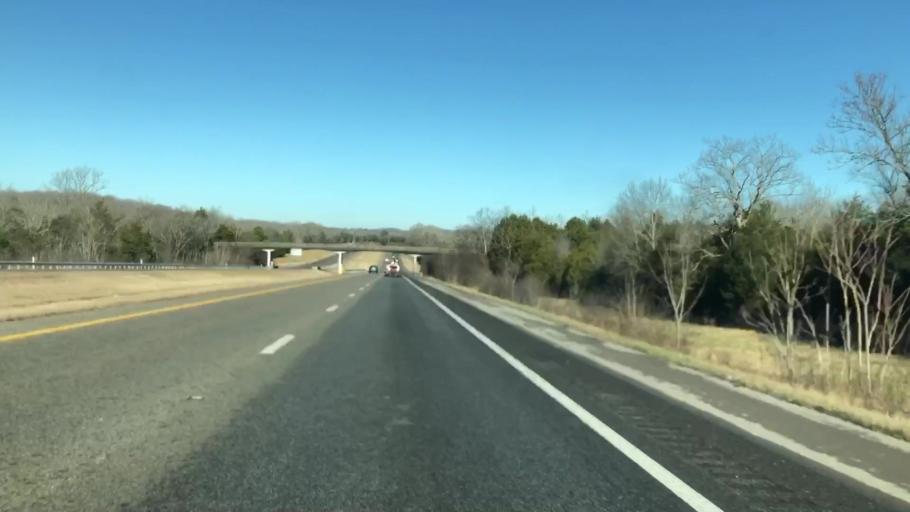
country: US
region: Tennessee
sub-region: Marshall County
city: Lewisburg
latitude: 35.5410
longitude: -86.9051
